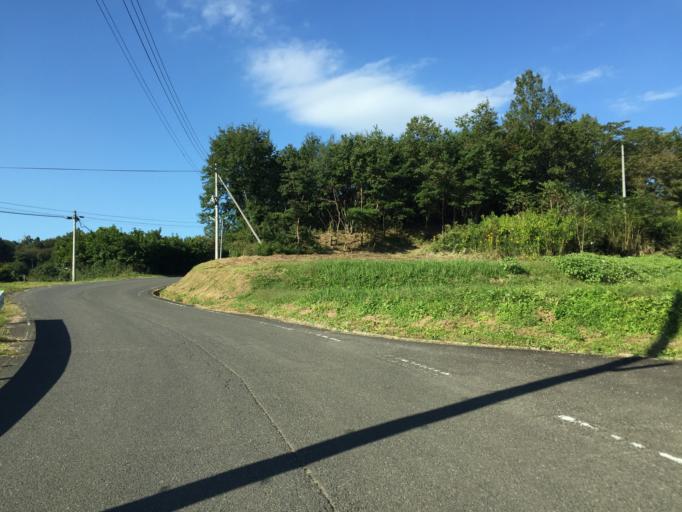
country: JP
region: Fukushima
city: Nihommatsu
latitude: 37.6476
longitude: 140.4971
